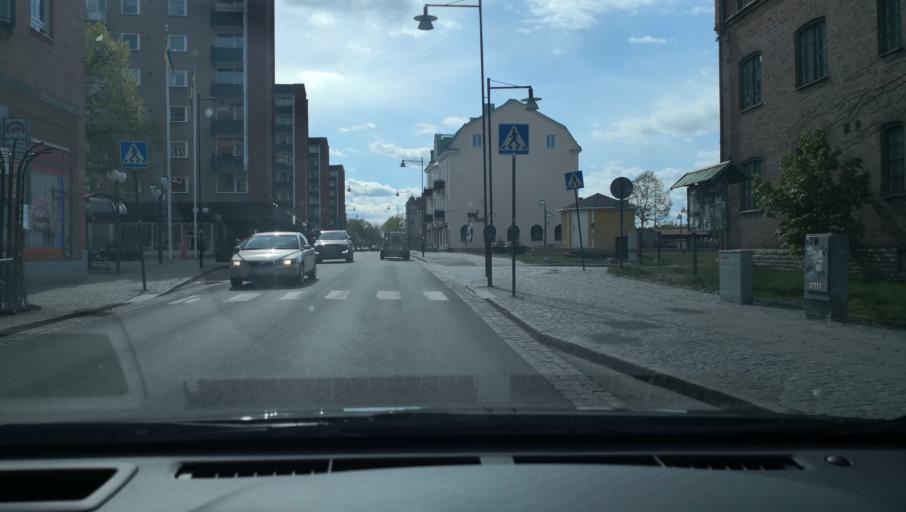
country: SE
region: OErebro
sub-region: Hallsbergs Kommun
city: Hallsberg
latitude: 59.0661
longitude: 15.1096
